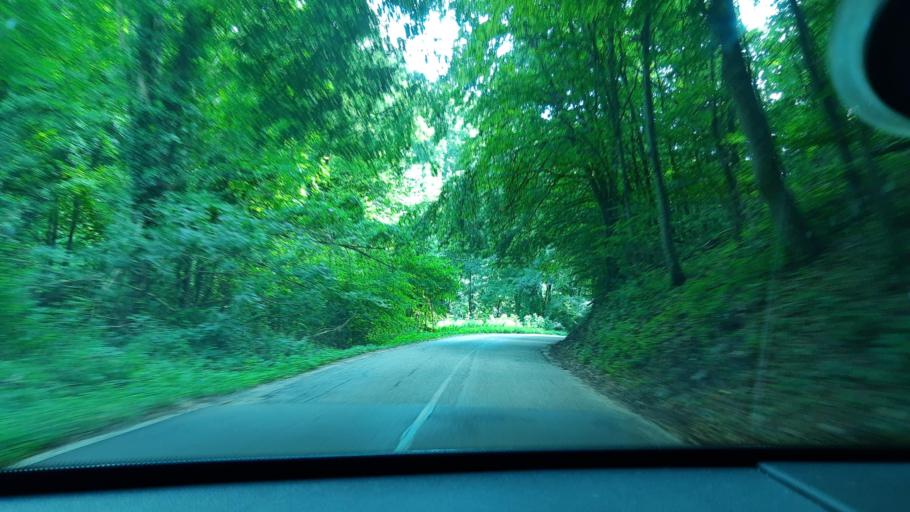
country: SK
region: Trnavsky
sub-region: Okres Trnava
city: Piestany
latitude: 48.6415
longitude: 17.9358
